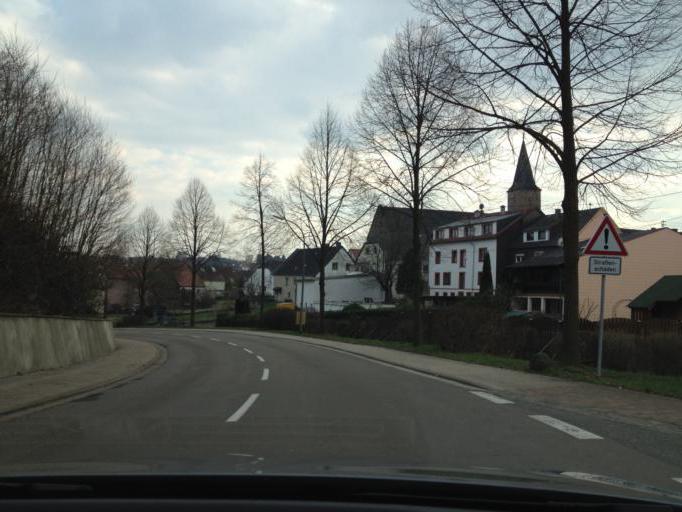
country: DE
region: Rheinland-Pfalz
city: Reichweiler
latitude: 49.5269
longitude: 7.2598
